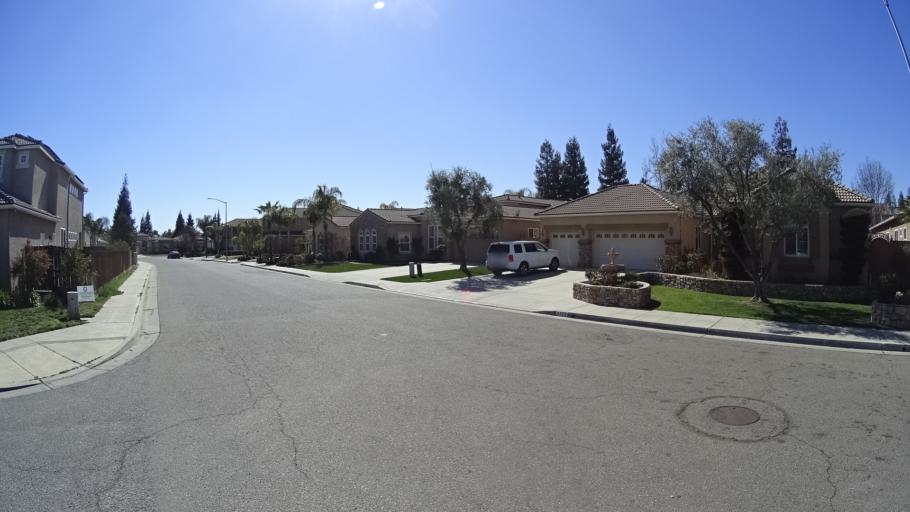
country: US
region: California
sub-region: Fresno County
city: Clovis
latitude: 36.8570
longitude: -119.7337
